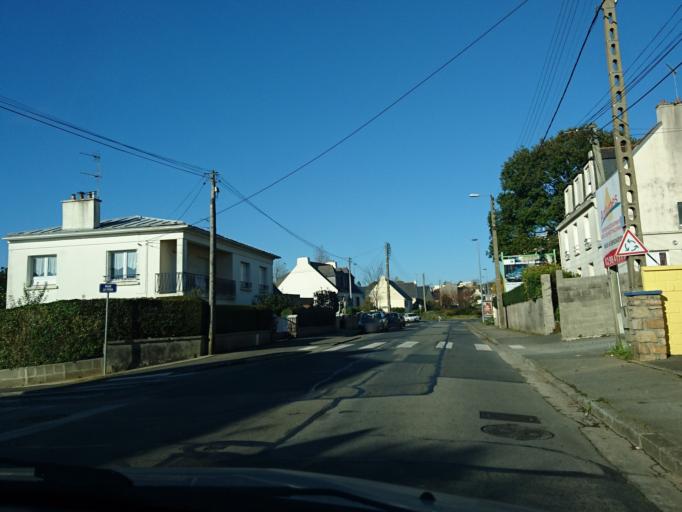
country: FR
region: Brittany
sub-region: Departement du Finistere
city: Brest
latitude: 48.4116
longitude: -4.4761
